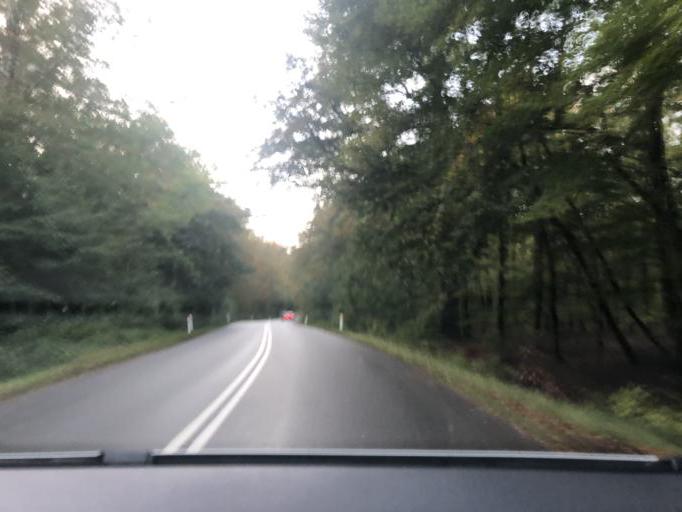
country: DK
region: Capital Region
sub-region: Frederikssund Kommune
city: Slangerup
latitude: 55.8164
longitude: 12.2033
